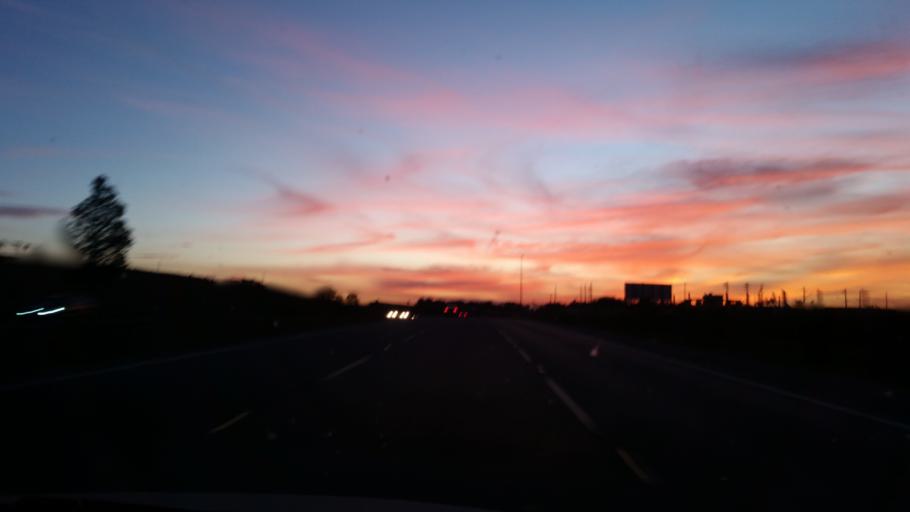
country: BR
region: Sao Paulo
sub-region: Guararema
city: Guararema
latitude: -23.3593
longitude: -46.0854
